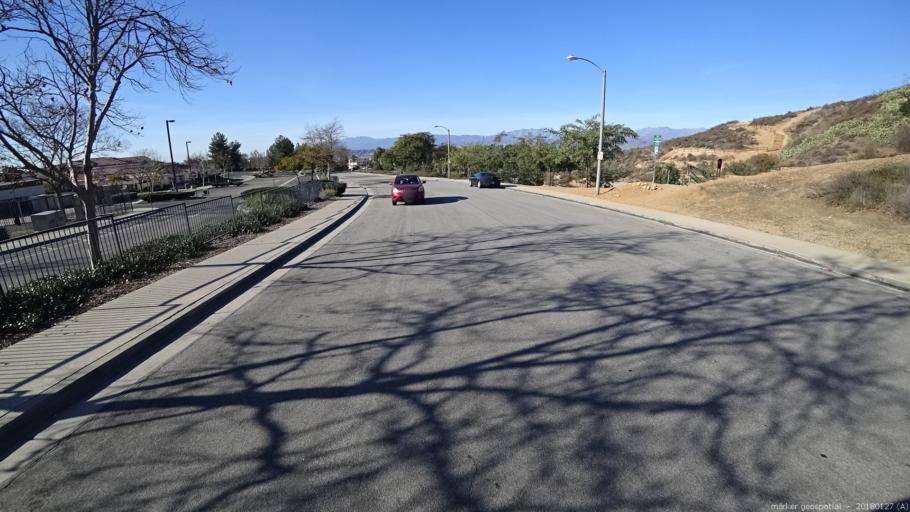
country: US
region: California
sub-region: Los Angeles County
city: Diamond Bar
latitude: 34.0112
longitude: -117.7902
